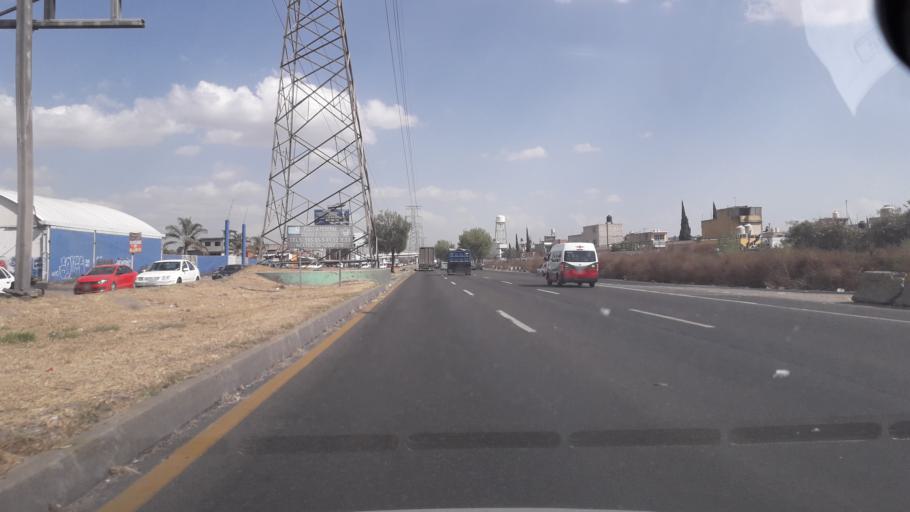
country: MX
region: Mexico
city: Santo Tomas Chiconautla
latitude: 19.6150
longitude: -99.0288
